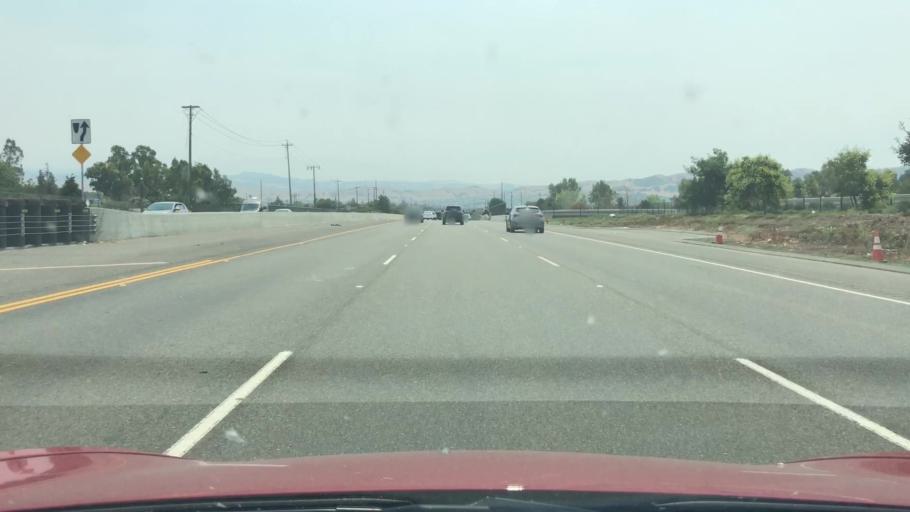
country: US
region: California
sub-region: Alameda County
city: Livermore
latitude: 37.6812
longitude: -121.8055
